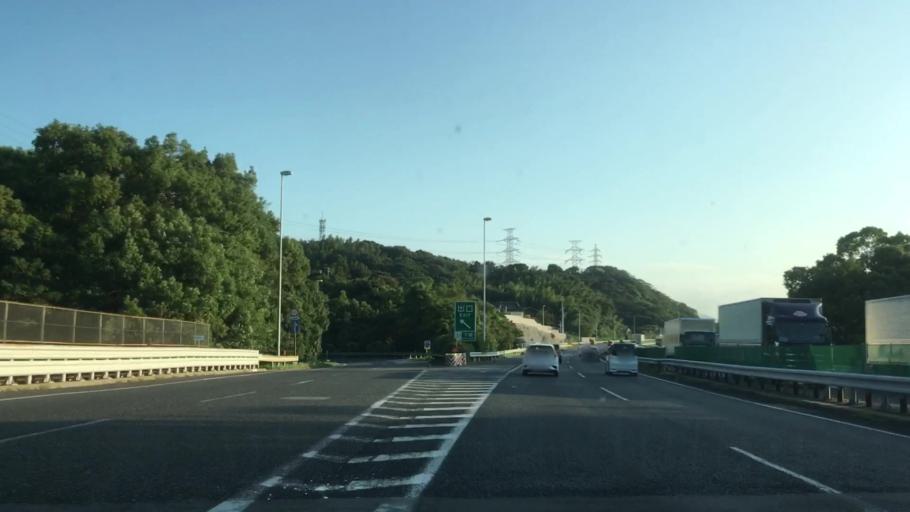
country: JP
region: Yamaguchi
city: Shimonoseki
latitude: 33.9788
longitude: 130.9525
